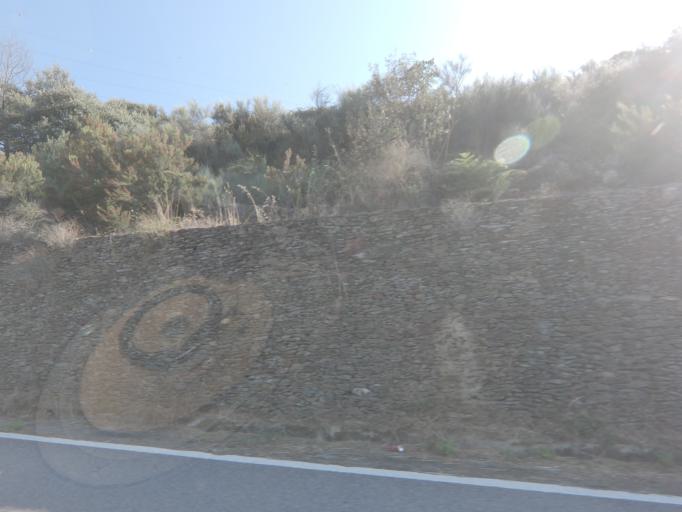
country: PT
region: Viseu
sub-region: Tabuaco
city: Tabuaco
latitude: 41.1491
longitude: -7.5793
